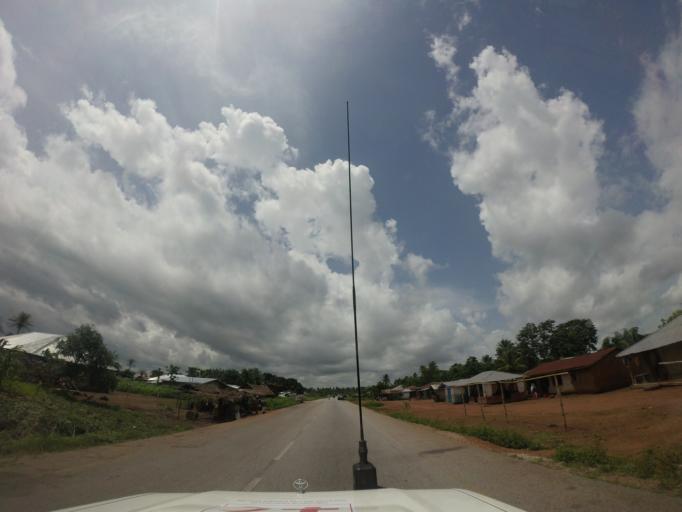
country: SL
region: Northern Province
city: Lunsar
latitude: 8.4854
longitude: -12.6070
